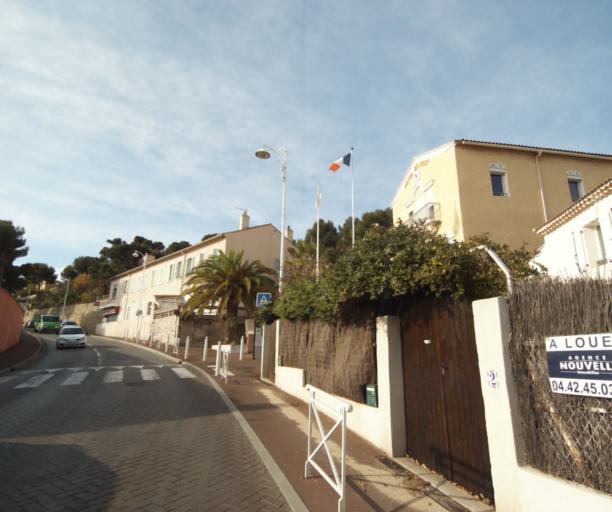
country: FR
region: Provence-Alpes-Cote d'Azur
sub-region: Departement des Bouches-du-Rhone
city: Carry-le-Rouet
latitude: 43.3306
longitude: 5.1515
